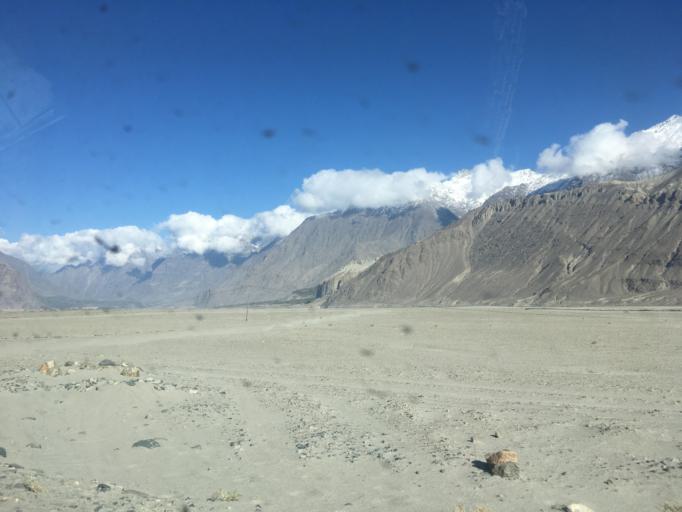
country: PK
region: Gilgit-Baltistan
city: Skardu
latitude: 35.3578
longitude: 75.5416
